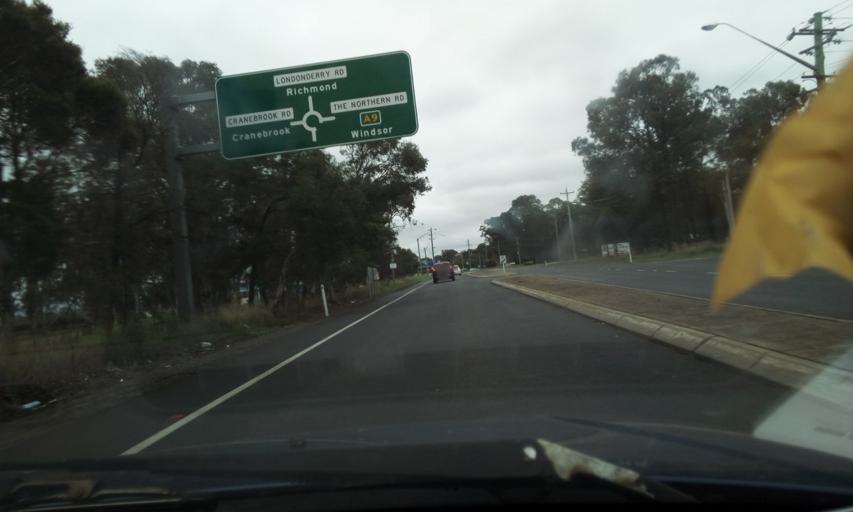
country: AU
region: New South Wales
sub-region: Penrith Municipality
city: Werrington Downs
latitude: -33.6919
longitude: 150.7279
